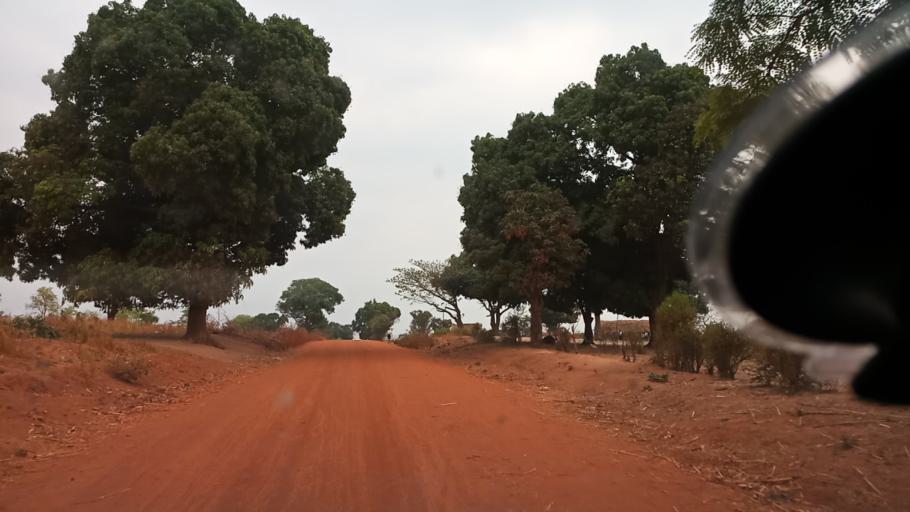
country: ZM
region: Luapula
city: Nchelenge
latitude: -9.1769
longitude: 28.2820
